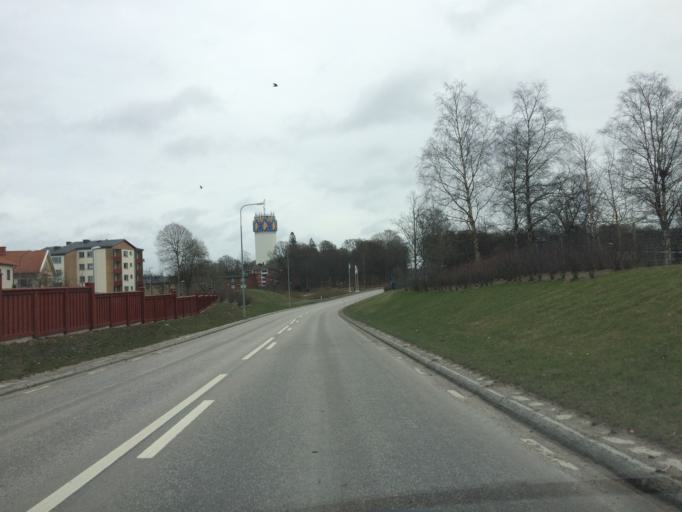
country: SE
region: Kronoberg
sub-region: Almhults Kommun
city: AElmhult
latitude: 56.5496
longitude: 14.1411
